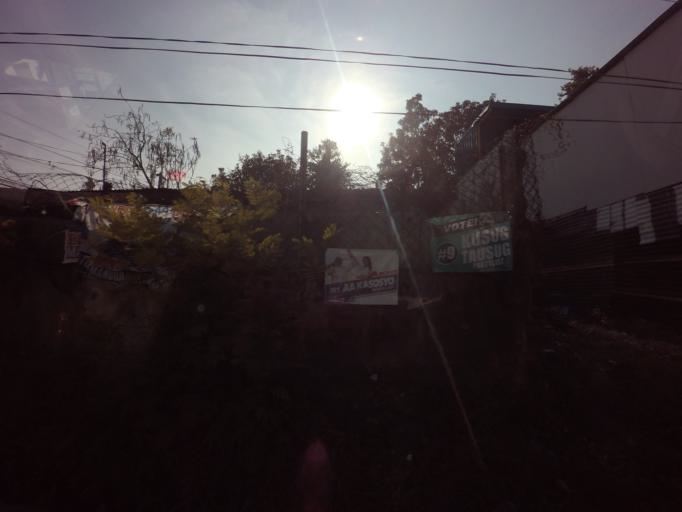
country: PH
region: Calabarzon
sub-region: Province of Rizal
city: Taguig
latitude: 14.4971
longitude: 121.0590
